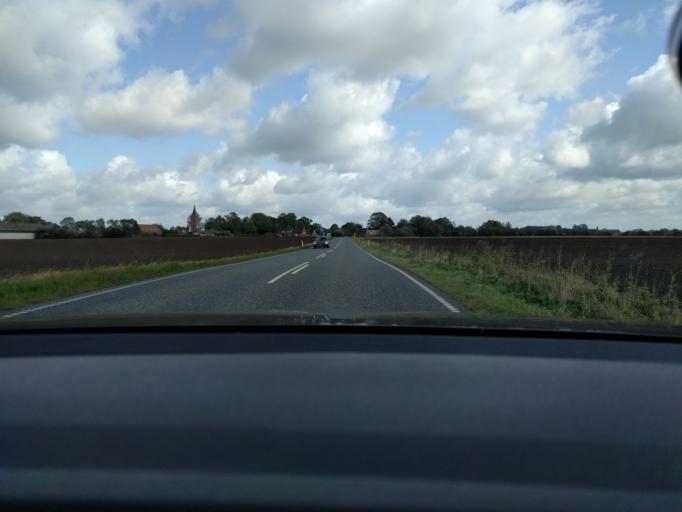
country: DK
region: Central Jutland
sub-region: Viborg Kommune
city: Bjerringbro
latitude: 56.3044
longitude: 9.7088
